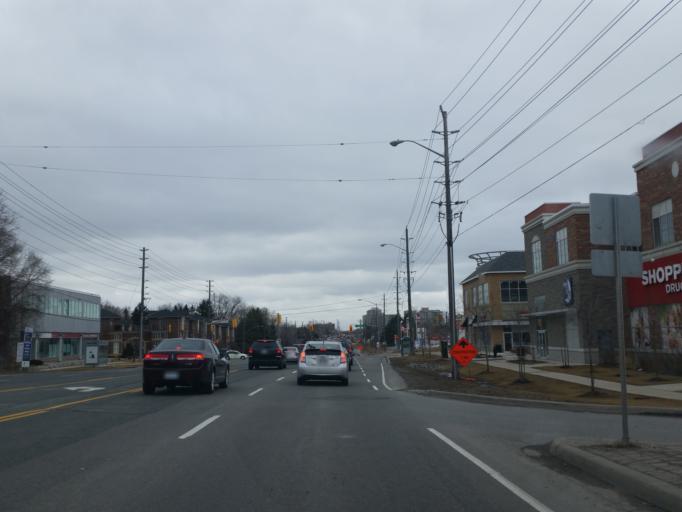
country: CA
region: Ontario
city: Ajax
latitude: 43.8302
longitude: -79.0973
